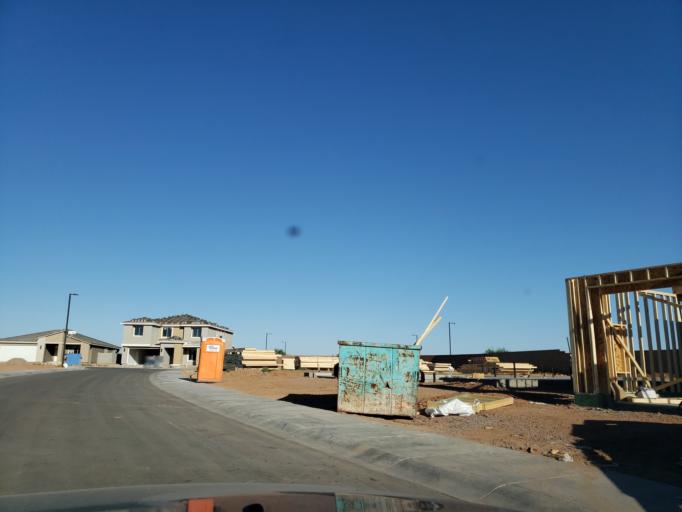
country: US
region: Arizona
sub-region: Maricopa County
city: Cave Creek
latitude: 33.6851
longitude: -112.0093
